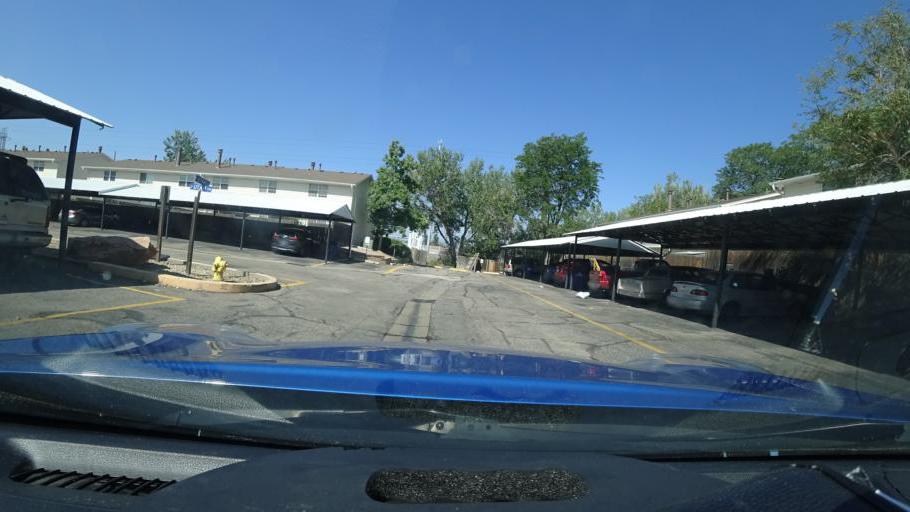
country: US
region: Colorado
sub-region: Adams County
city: Aurora
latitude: 39.6836
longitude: -104.8258
